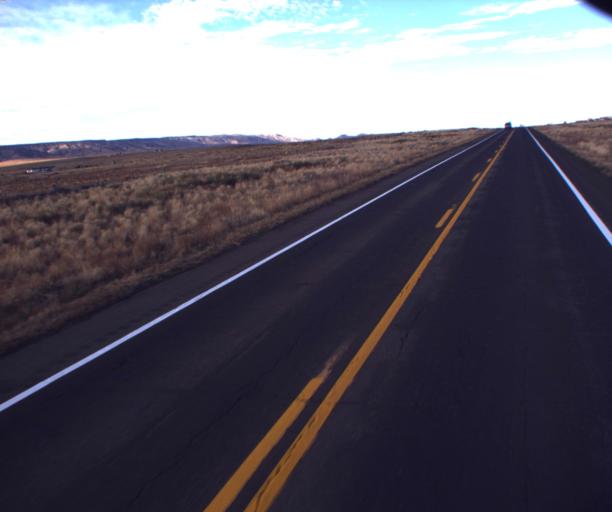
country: US
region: Arizona
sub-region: Apache County
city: Lukachukai
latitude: 36.9591
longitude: -109.3291
